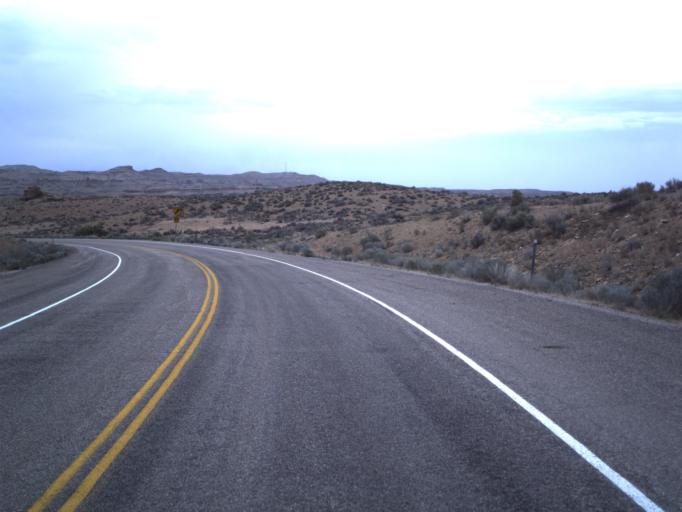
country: US
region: Colorado
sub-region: Rio Blanco County
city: Rangely
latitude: 39.9612
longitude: -109.1621
